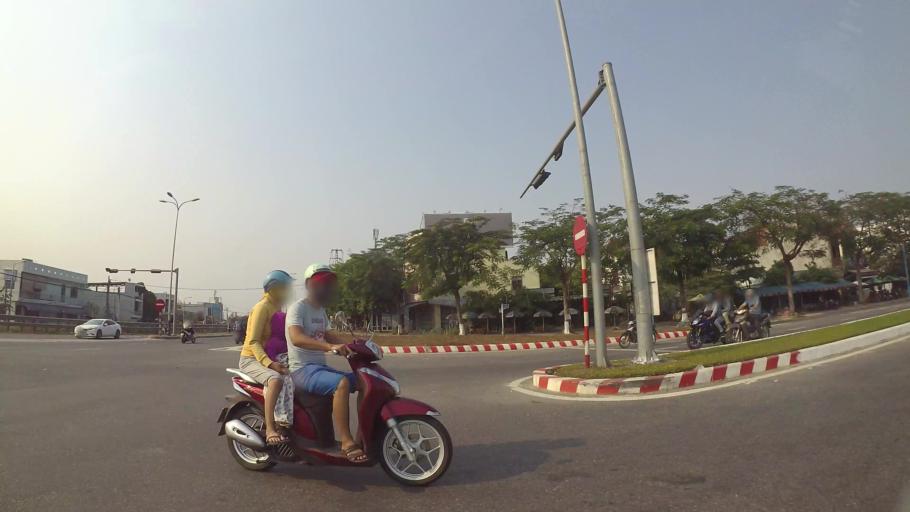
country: VN
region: Da Nang
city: Cam Le
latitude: 16.0202
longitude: 108.1942
